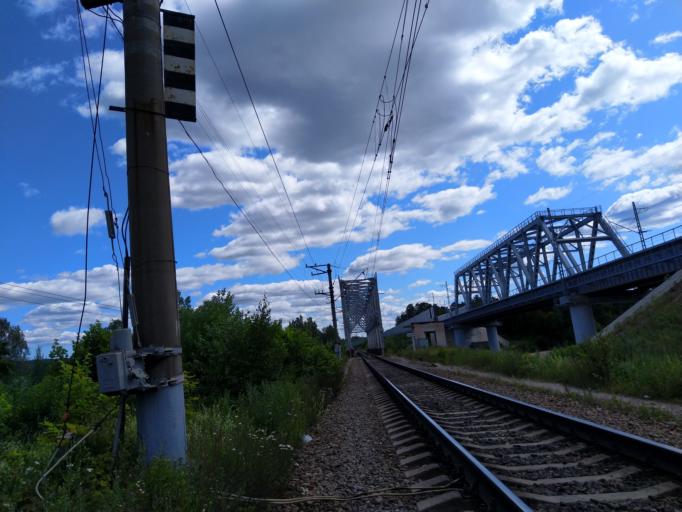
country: RU
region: Leningrad
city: Sapernoye
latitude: 60.6831
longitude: 30.0078
